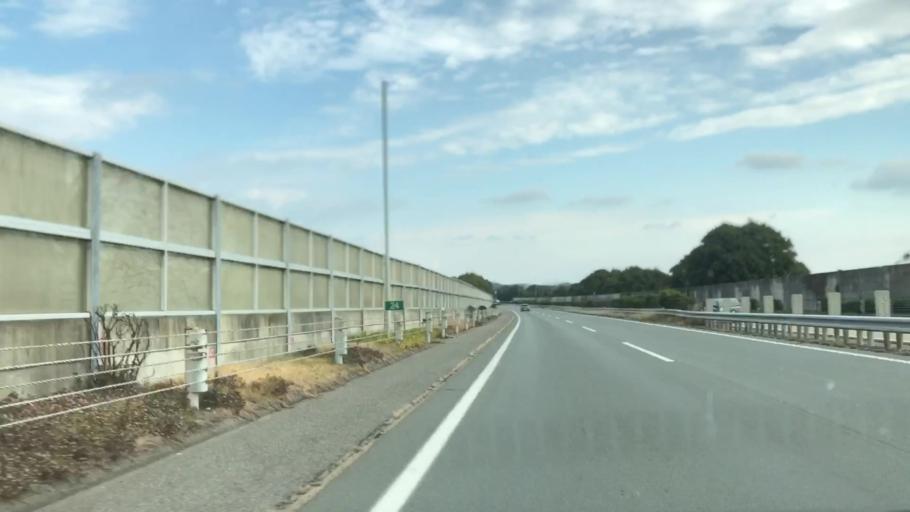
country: JP
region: Saga Prefecture
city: Kanzakimachi-kanzaki
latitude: 33.3288
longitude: 130.3037
